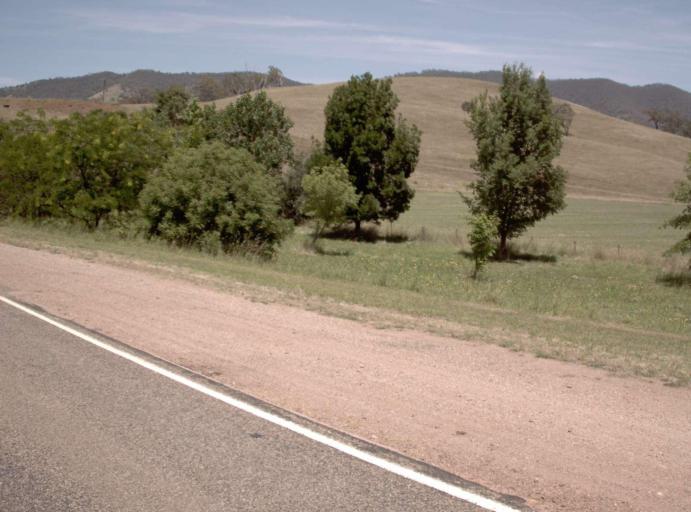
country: AU
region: Victoria
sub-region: East Gippsland
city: Bairnsdale
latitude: -37.3815
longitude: 147.8304
